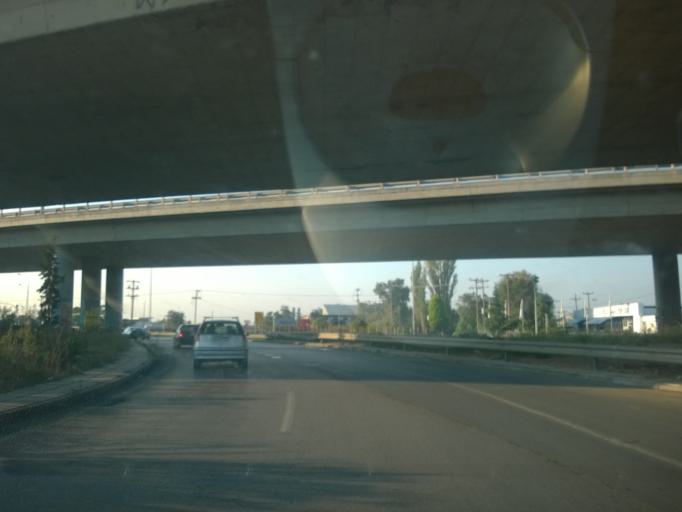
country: GR
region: Central Macedonia
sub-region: Nomos Thessalonikis
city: Menemeni
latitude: 40.6535
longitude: 22.8997
